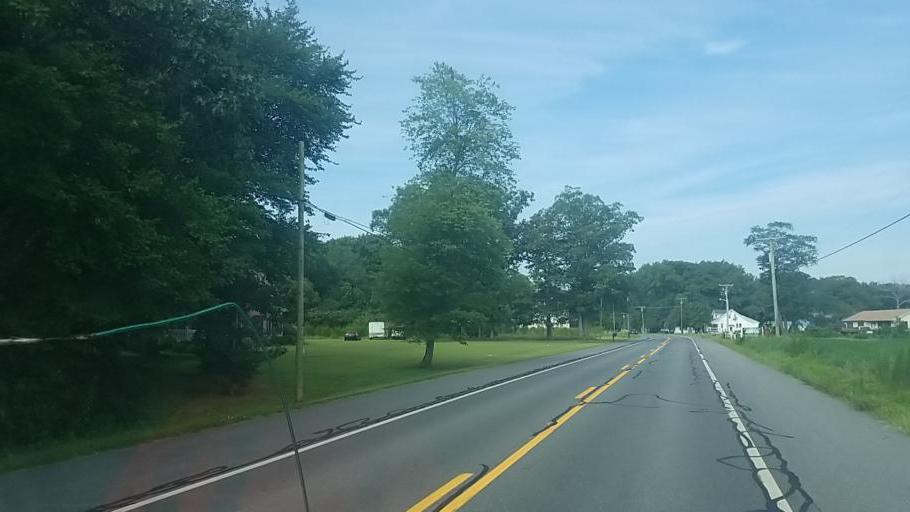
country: US
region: Delaware
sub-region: Sussex County
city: Selbyville
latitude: 38.5274
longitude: -75.2061
